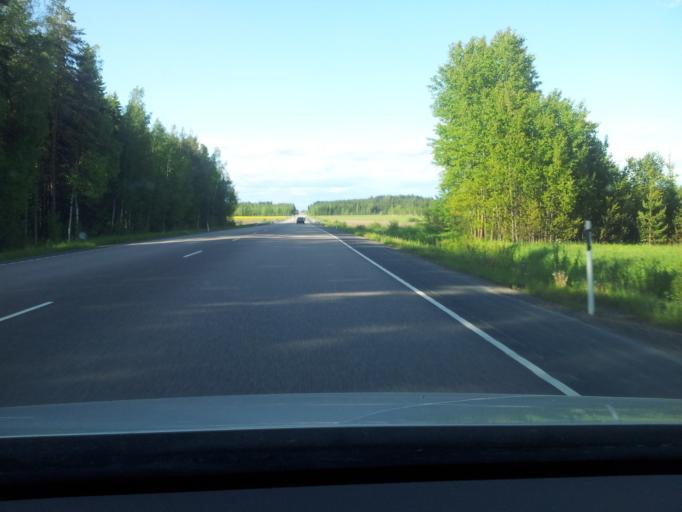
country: FI
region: Kymenlaakso
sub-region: Kouvola
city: Elimaeki
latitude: 60.7971
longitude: 26.5073
